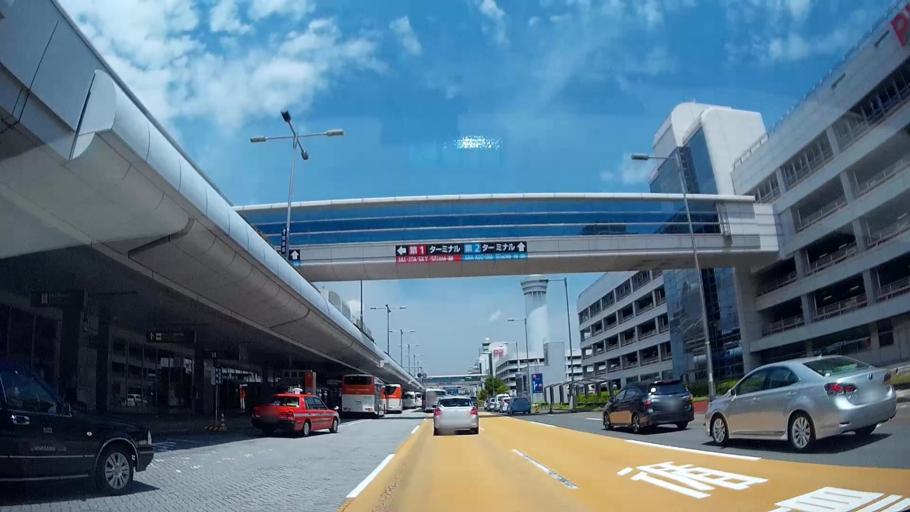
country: JP
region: Kanagawa
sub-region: Kawasaki-shi
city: Kawasaki
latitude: 35.5480
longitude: 139.7854
